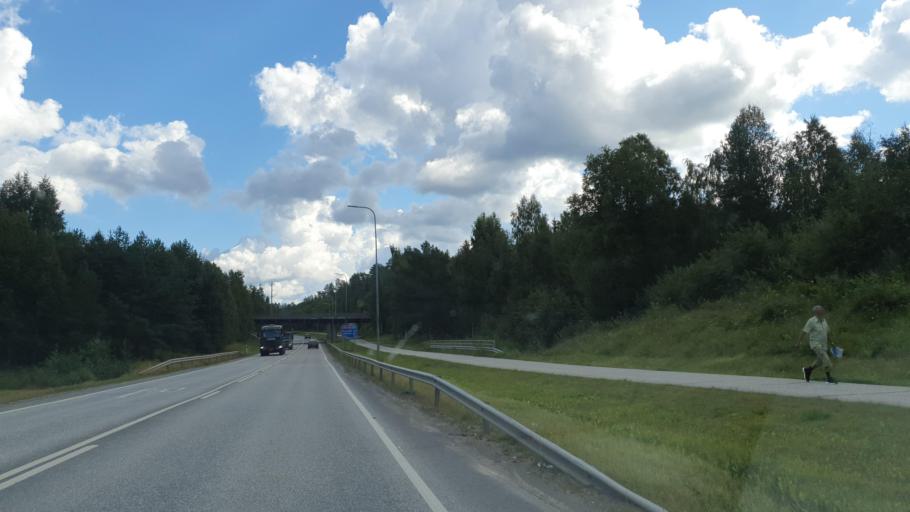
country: FI
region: Kainuu
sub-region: Kajaani
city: Kajaani
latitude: 64.2181
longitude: 27.6950
